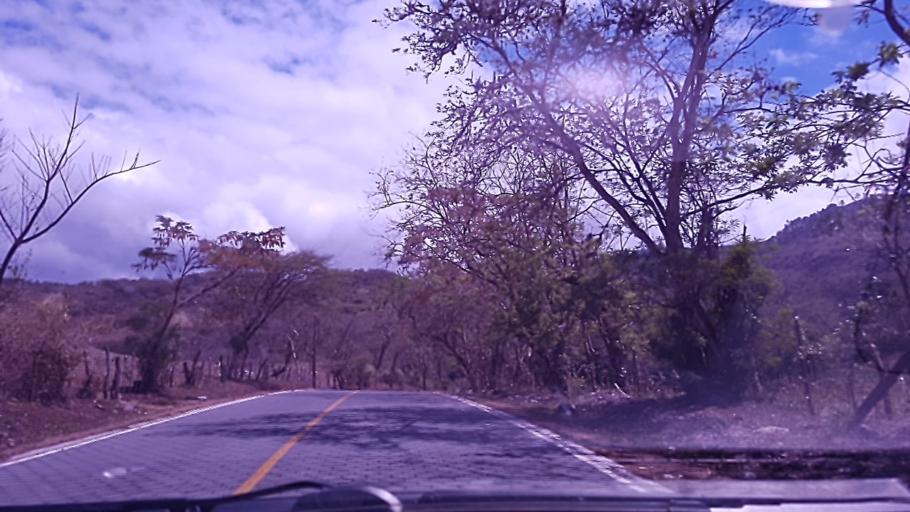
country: NI
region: Esteli
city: Condega
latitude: 13.4044
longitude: -86.2946
